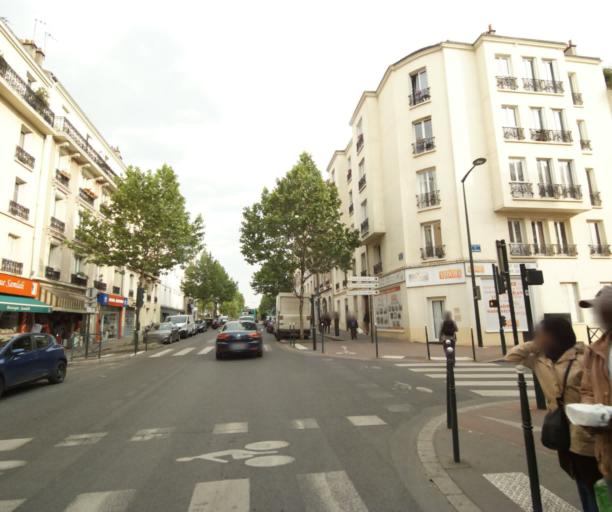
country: FR
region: Ile-de-France
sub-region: Departement des Hauts-de-Seine
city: Clichy
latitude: 48.9074
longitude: 2.2968
